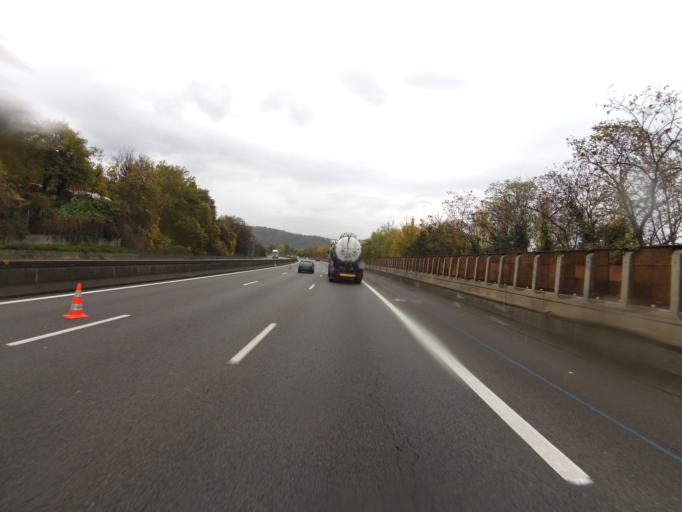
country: FR
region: Rhone-Alpes
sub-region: Departement du Rhone
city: Saint-Romain-en-Gal
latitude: 45.5284
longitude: 4.8619
